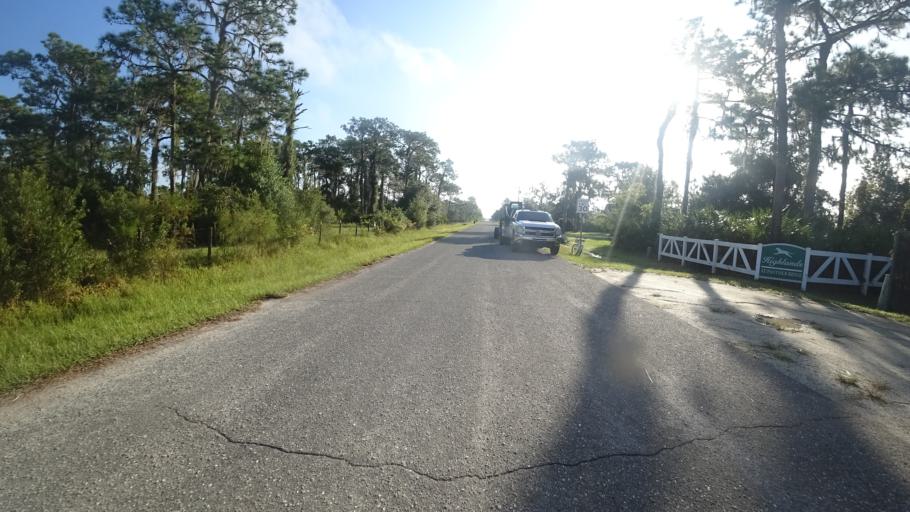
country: US
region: Florida
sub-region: Sarasota County
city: Fruitville
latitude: 27.4017
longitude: -82.3038
